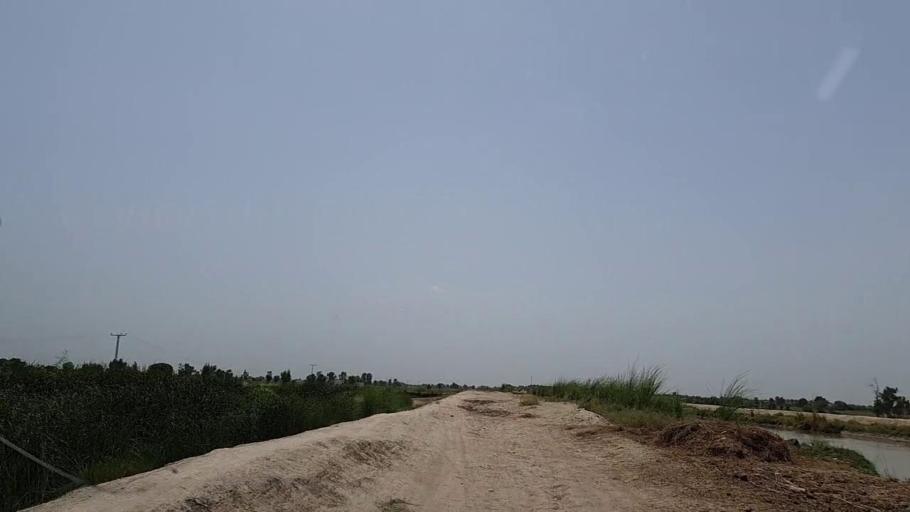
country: PK
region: Sindh
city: Tharu Shah
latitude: 26.9910
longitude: 68.0970
